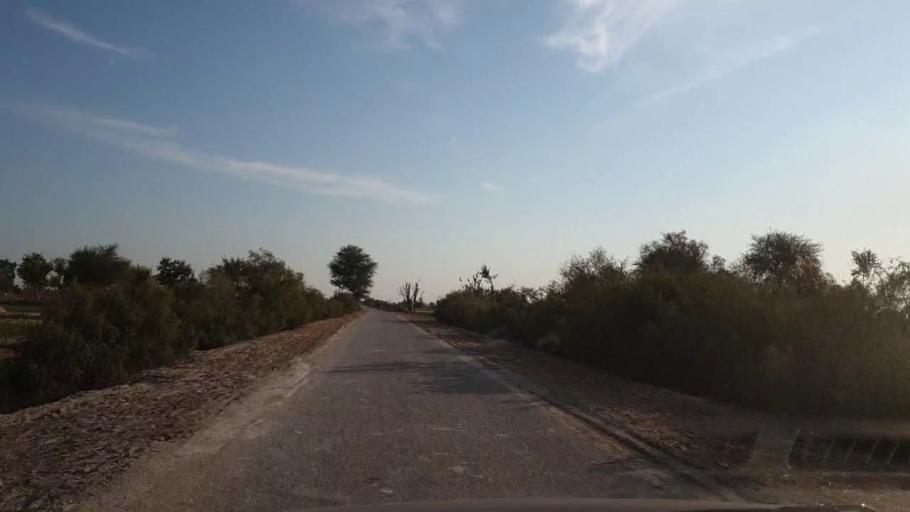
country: PK
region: Sindh
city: Khadro
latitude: 26.2022
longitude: 68.7467
